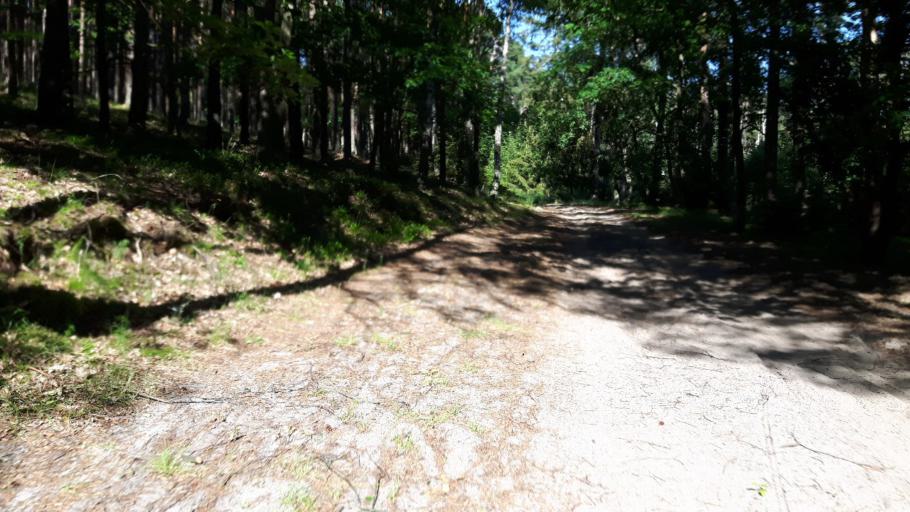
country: PL
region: Pomeranian Voivodeship
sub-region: Powiat leborski
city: Leba
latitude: 54.7042
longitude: 17.5224
